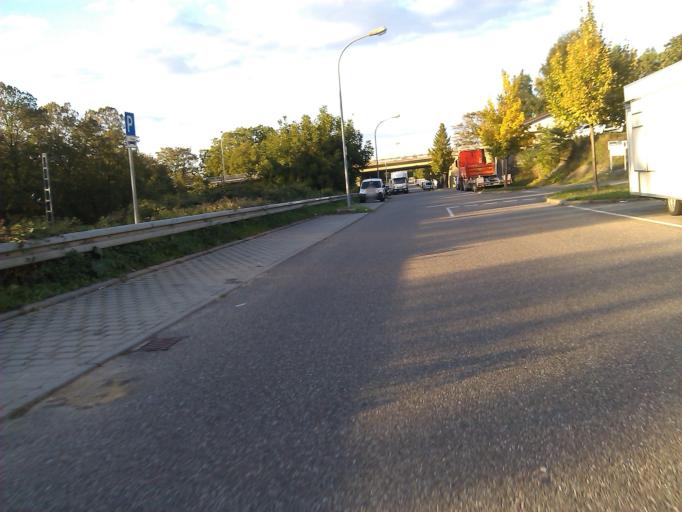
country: DE
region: Baden-Wuerttemberg
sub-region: Regierungsbezirk Stuttgart
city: Heilbronn
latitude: 49.1572
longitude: 9.2232
